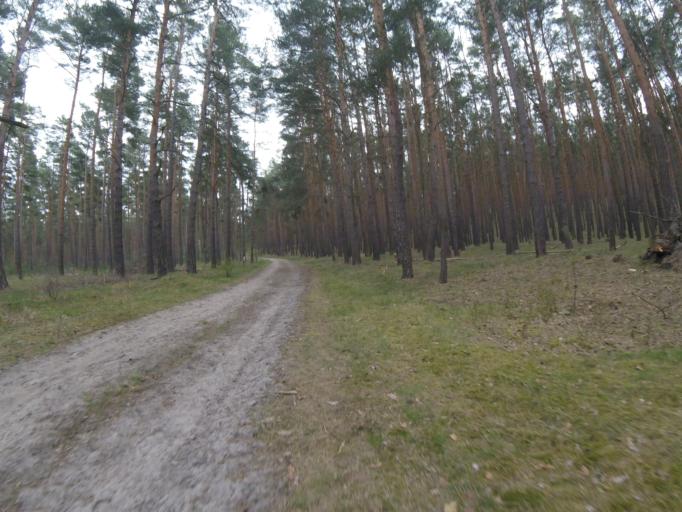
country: DE
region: Brandenburg
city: Schwerin
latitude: 52.1437
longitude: 13.6393
